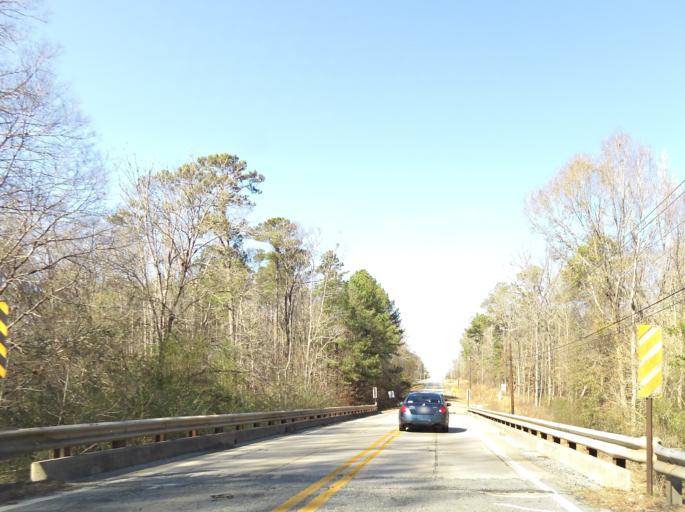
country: US
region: Georgia
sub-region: Bibb County
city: West Point
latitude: 32.8606
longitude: -83.7505
